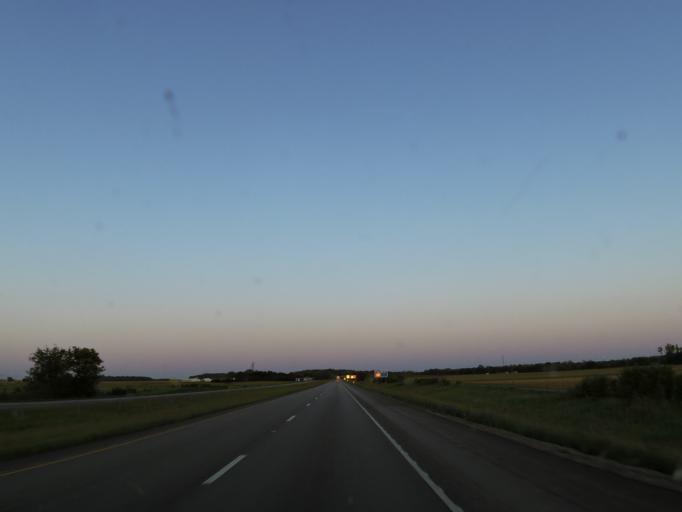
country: US
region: Indiana
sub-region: Montgomery County
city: Crawfordsville
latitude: 40.0607
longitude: -86.8350
